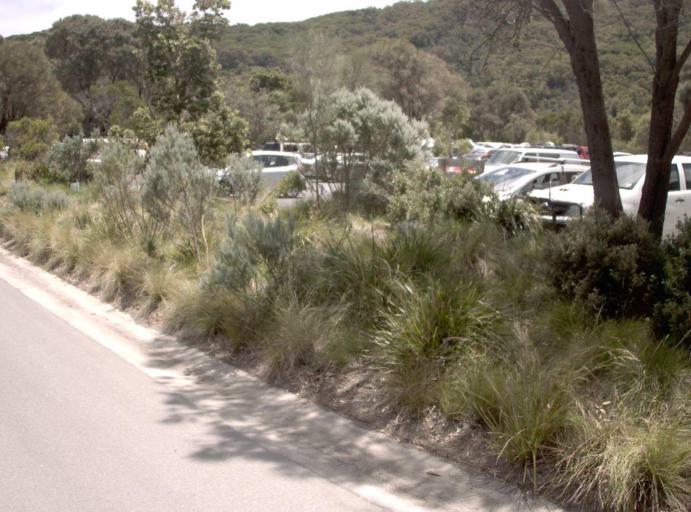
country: AU
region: Victoria
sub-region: Latrobe
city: Morwell
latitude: -39.0306
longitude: 146.3223
